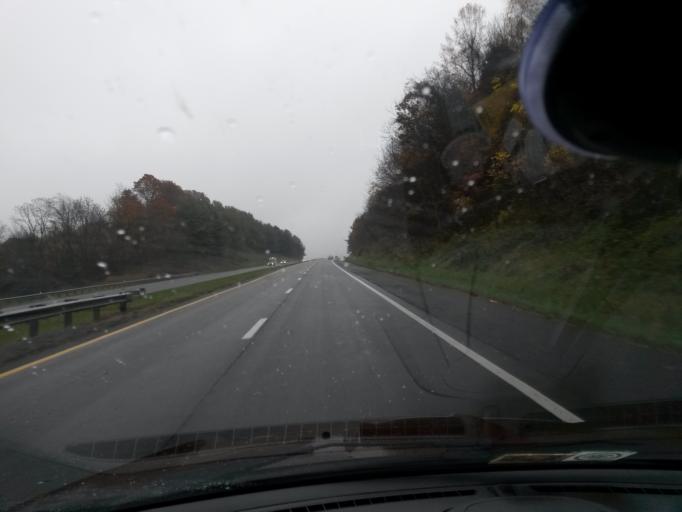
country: US
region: Virginia
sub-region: Montgomery County
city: Christiansburg
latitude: 37.1410
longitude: -80.3847
